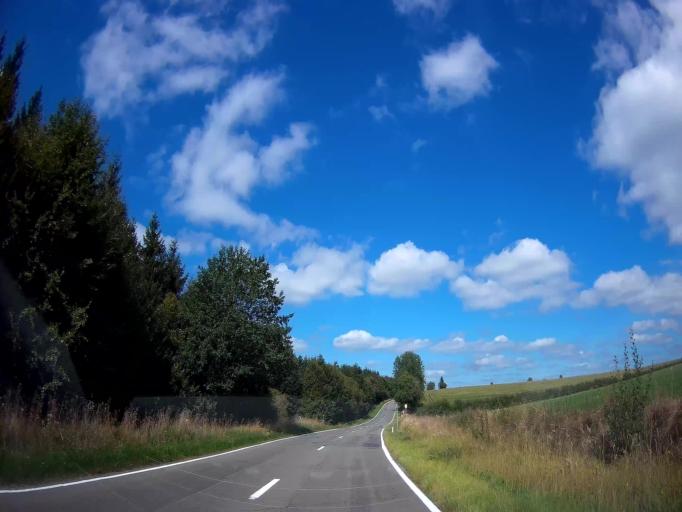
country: BE
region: Wallonia
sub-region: Province du Luxembourg
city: Bastogne
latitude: 50.0379
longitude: 5.6925
